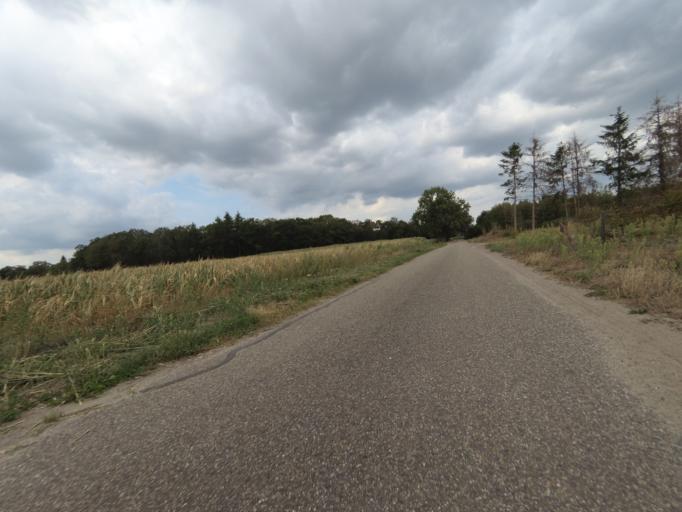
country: NL
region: Overijssel
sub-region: Gemeente Haaksbergen
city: Haaksbergen
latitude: 52.1871
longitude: 6.7526
